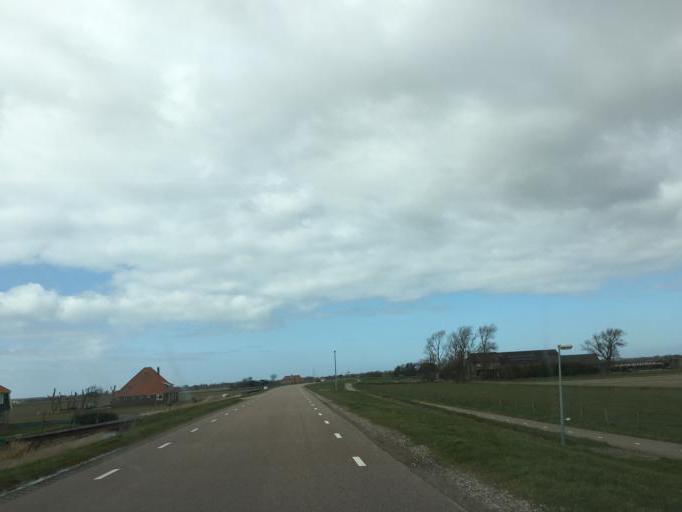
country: NL
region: North Holland
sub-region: Gemeente Schagen
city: Schagen
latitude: 52.8502
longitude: 4.7390
